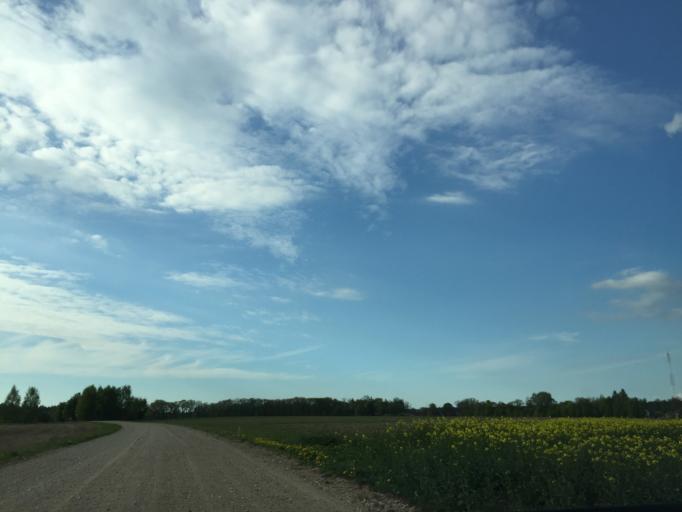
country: LV
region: Limbazu Rajons
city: Limbazi
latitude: 57.3713
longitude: 24.6899
